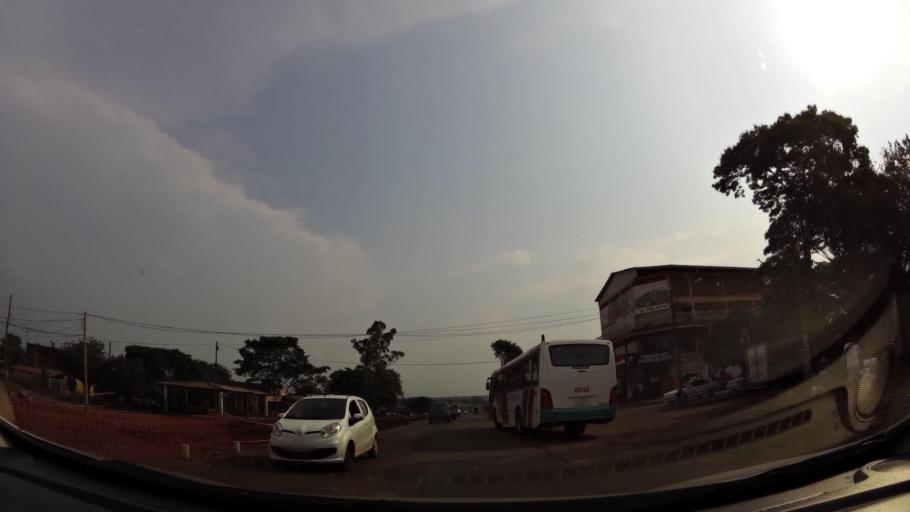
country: PY
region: Alto Parana
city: Ciudad del Este
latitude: -25.4856
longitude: -54.6610
